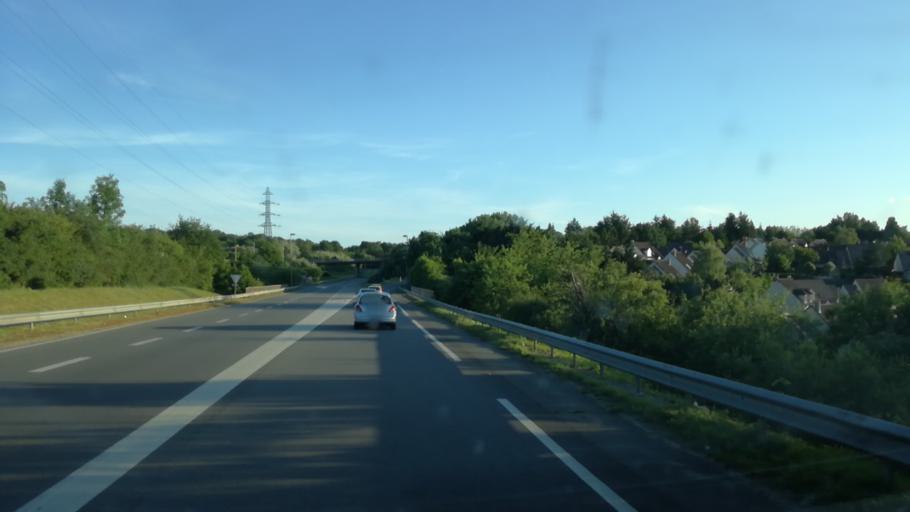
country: FR
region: Ile-de-France
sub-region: Departement des Yvelines
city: Elancourt
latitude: 48.7794
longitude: 1.9715
